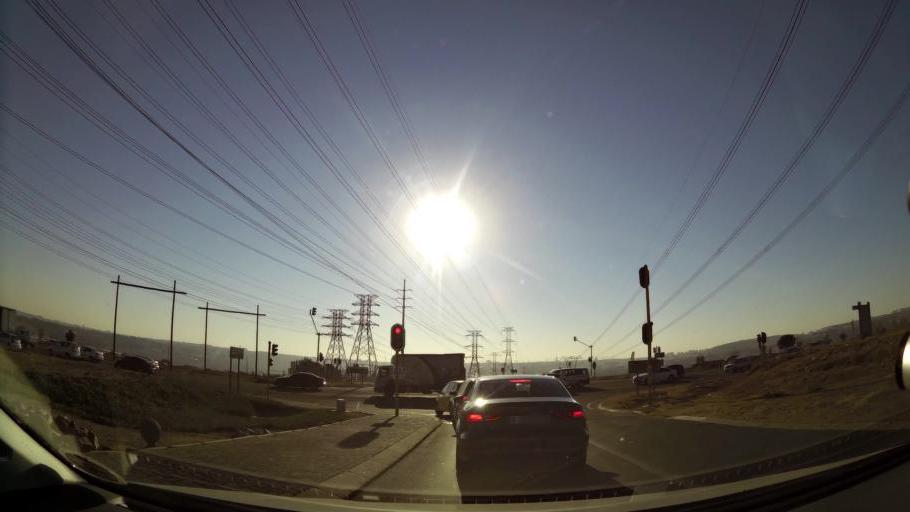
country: ZA
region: Gauteng
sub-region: City of Johannesburg Metropolitan Municipality
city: Modderfontein
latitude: -26.0432
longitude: 28.1482
